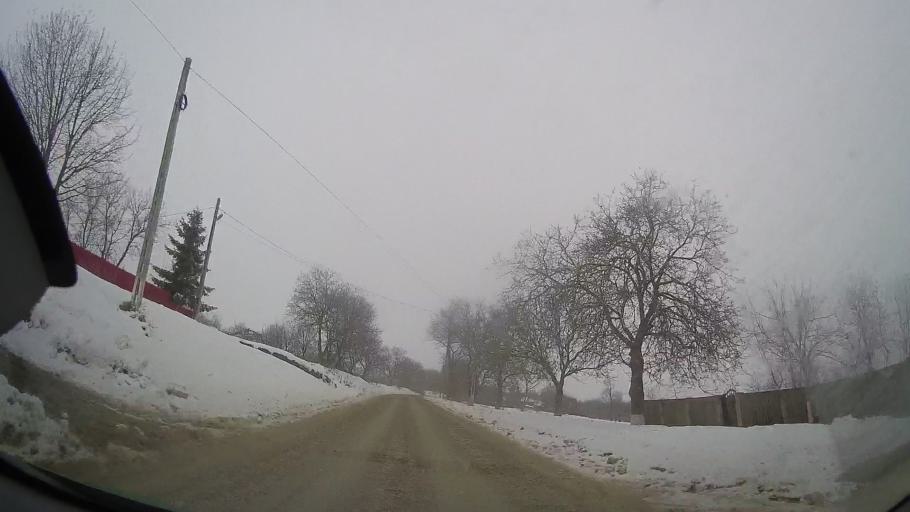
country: RO
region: Vaslui
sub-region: Comuna Todiresti
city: Todiresti
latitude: 46.8743
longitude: 27.3786
